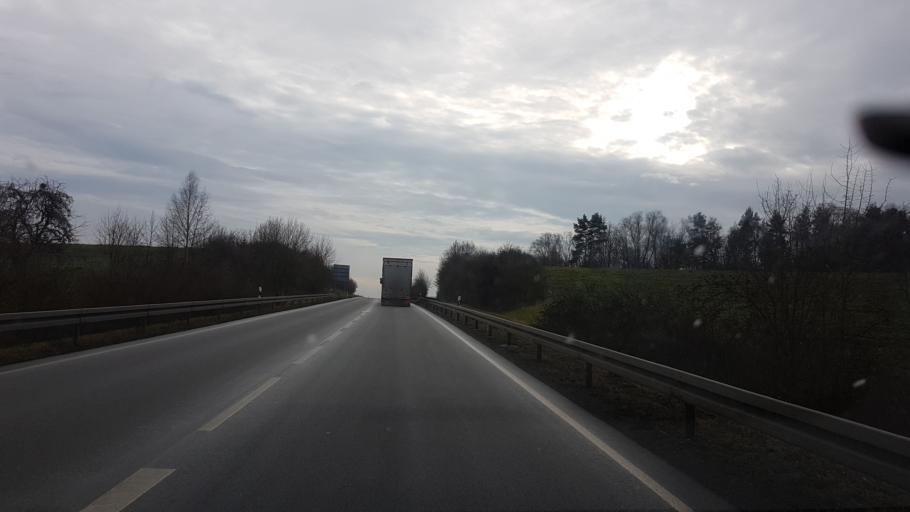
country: DE
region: Bavaria
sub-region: Upper Franconia
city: Reckendorf
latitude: 50.0320
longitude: 10.8255
